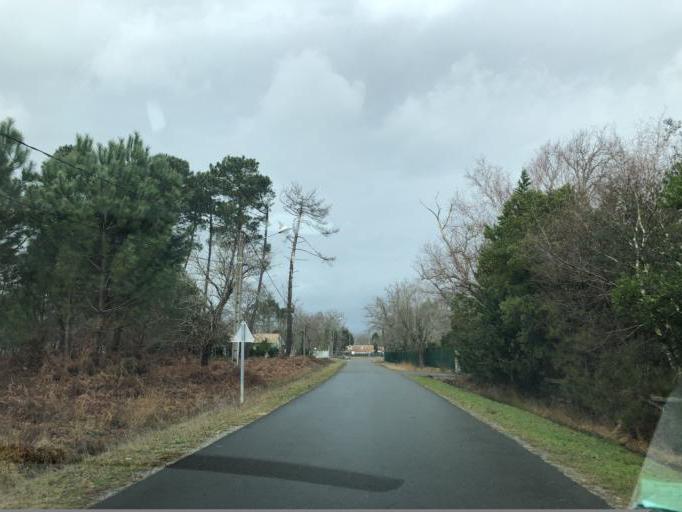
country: FR
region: Aquitaine
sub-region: Departement de la Gironde
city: Hourtin
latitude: 45.1798
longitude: -1.0751
